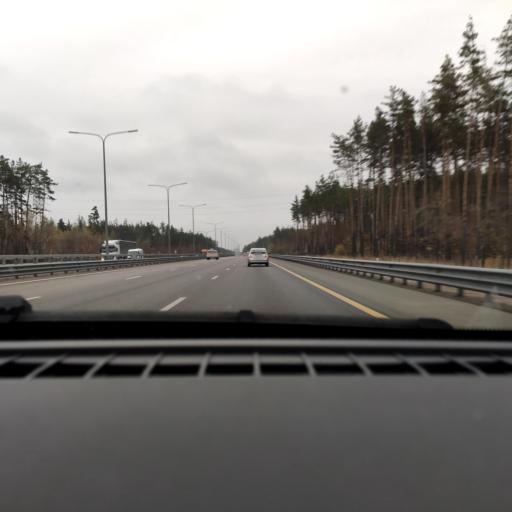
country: RU
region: Voronezj
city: Somovo
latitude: 51.7041
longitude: 39.3060
